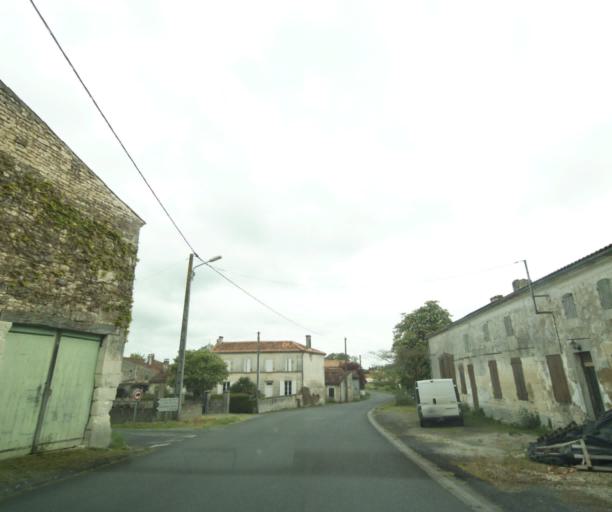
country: FR
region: Poitou-Charentes
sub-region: Departement de la Charente-Maritime
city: Chaniers
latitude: 45.6991
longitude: -0.5443
